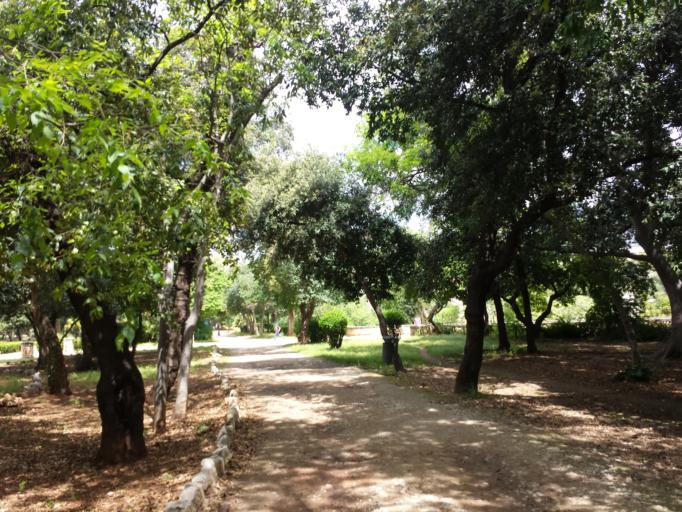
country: IT
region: Sicily
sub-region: Palermo
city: Palermo
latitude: 38.1294
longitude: 13.3484
